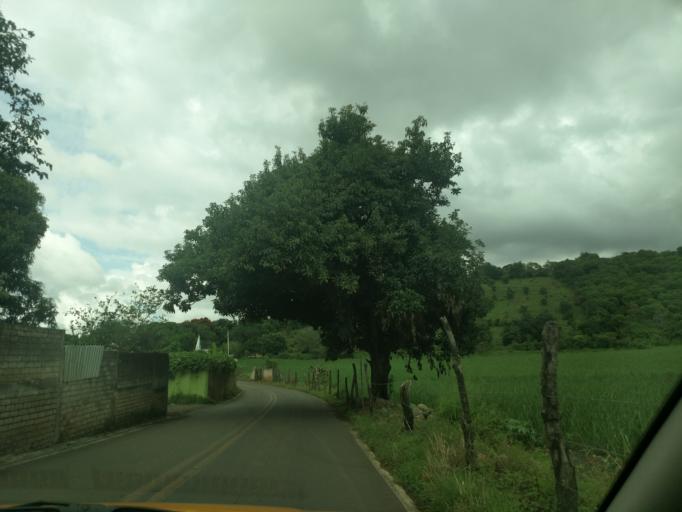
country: MX
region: Nayarit
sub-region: Tepic
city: La Corregidora
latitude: 21.4605
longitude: -104.7994
